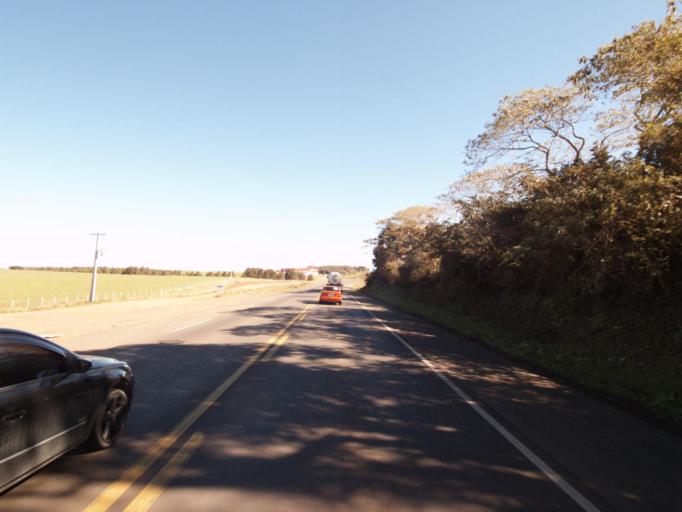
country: BR
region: Santa Catarina
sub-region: Xanxere
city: Xanxere
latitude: -26.8740
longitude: -52.2814
